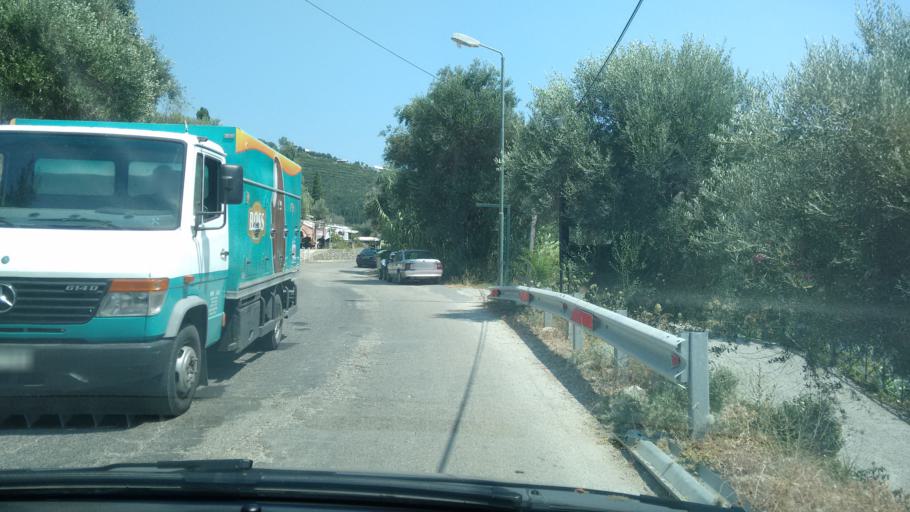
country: GR
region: Ionian Islands
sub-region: Nomos Kerkyras
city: Agios Georgis
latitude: 39.6752
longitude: 19.7219
